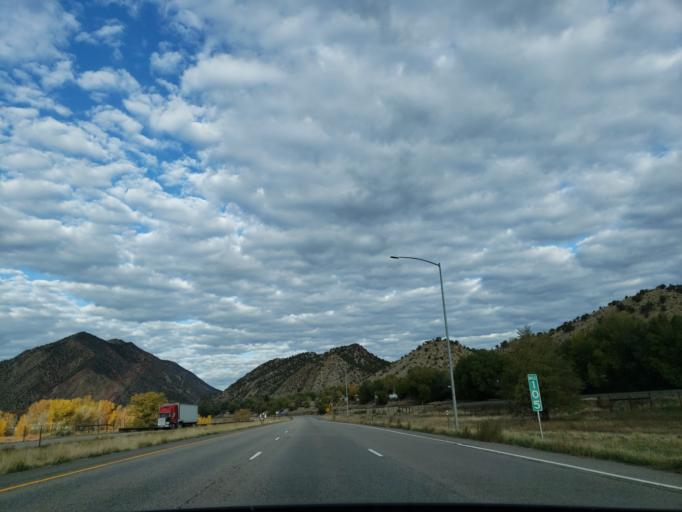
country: US
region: Colorado
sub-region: Garfield County
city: New Castle
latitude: 39.5676
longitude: -107.5208
